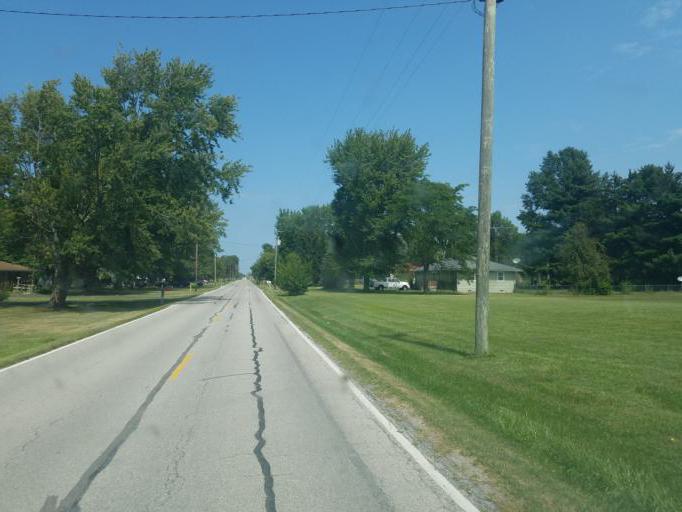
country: US
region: Ohio
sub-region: Marion County
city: Marion
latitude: 40.6164
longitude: -83.2173
